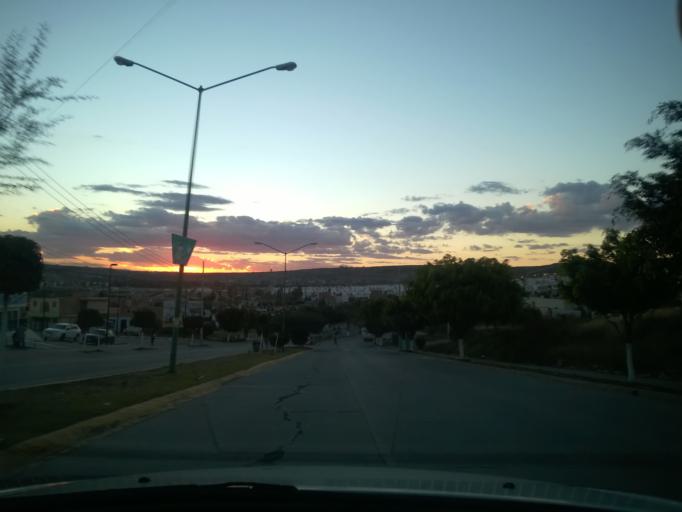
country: MX
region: Guanajuato
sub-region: Leon
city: La Ermita
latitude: 21.1559
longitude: -101.7375
